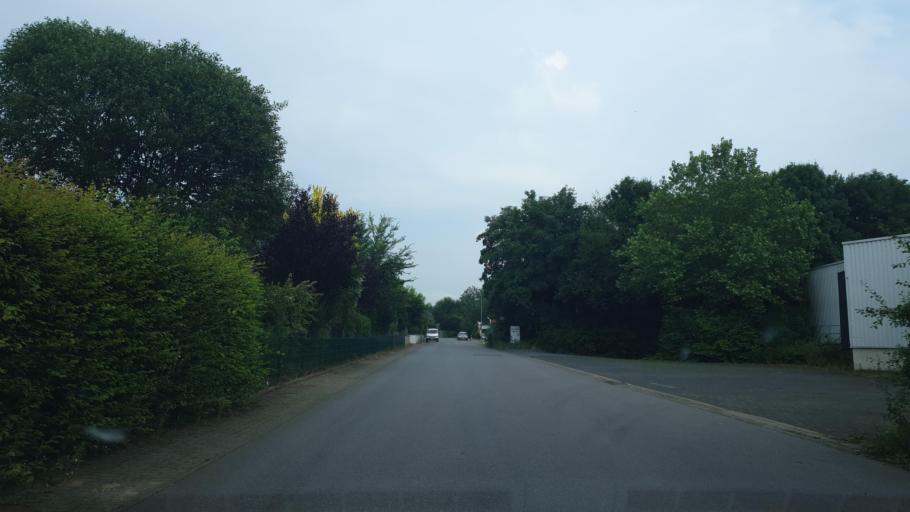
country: DE
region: North Rhine-Westphalia
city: Bad Oeynhausen
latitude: 52.2413
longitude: 8.7472
